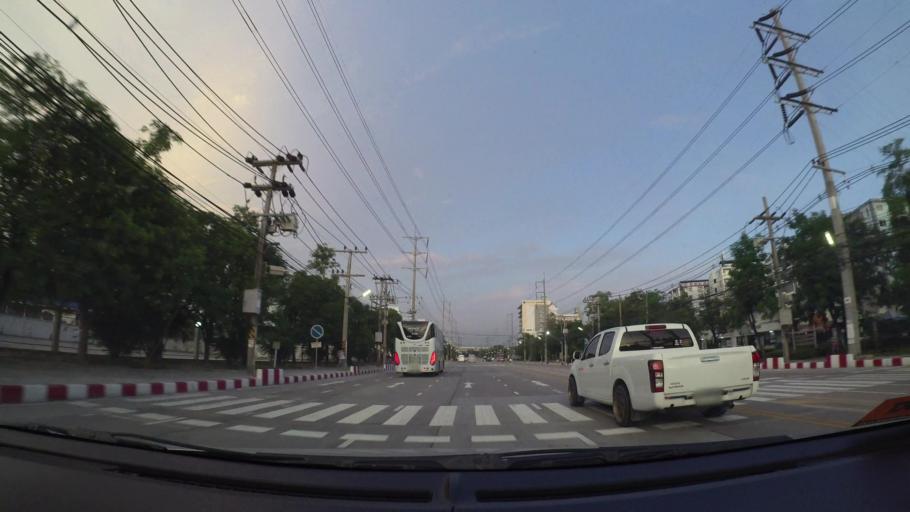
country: TH
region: Chon Buri
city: Chon Buri
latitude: 13.4233
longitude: 101.0008
